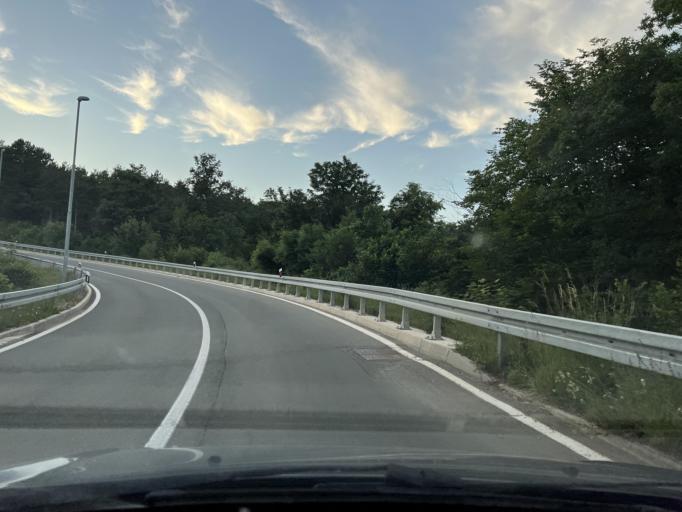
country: HR
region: Primorsko-Goranska
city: Marcelji
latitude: 45.4010
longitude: 14.3916
